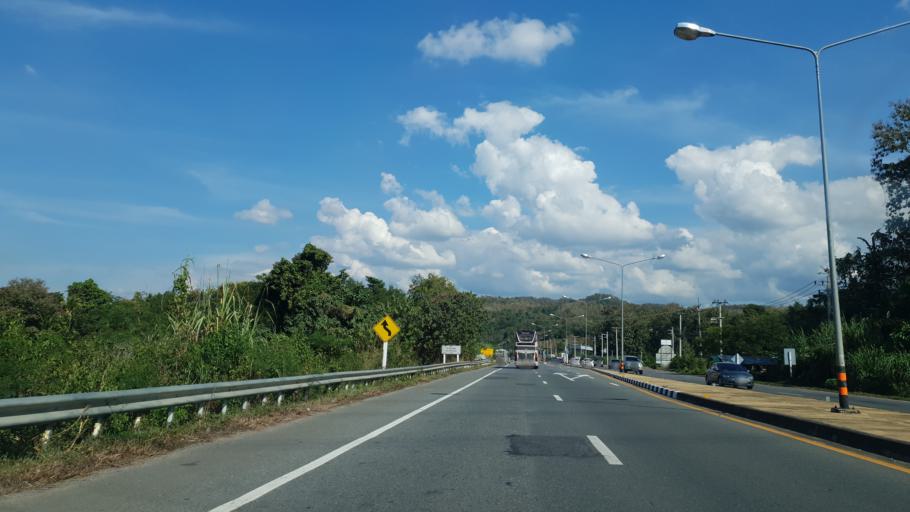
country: TH
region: Phrae
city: Den Chai
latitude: 17.9010
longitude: 100.0576
